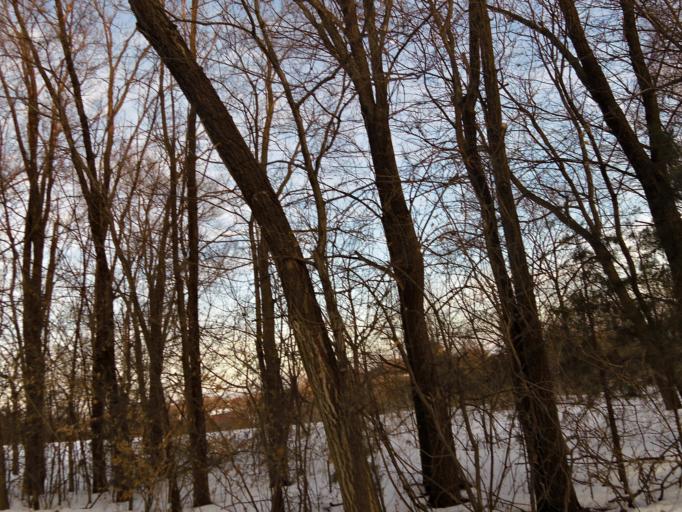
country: US
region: Wisconsin
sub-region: Saint Croix County
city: Hudson
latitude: 44.9744
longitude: -92.7412
